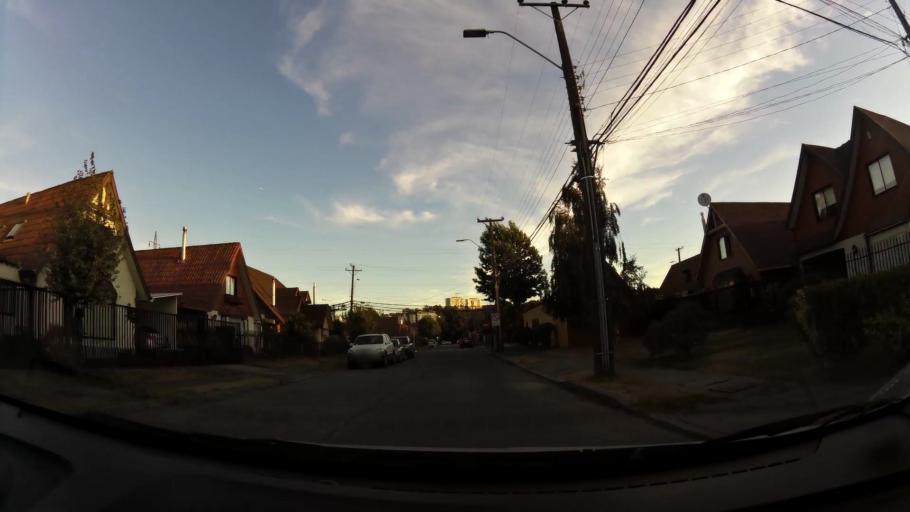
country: CL
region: Biobio
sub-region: Provincia de Concepcion
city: Concepcion
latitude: -36.8406
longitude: -73.0983
